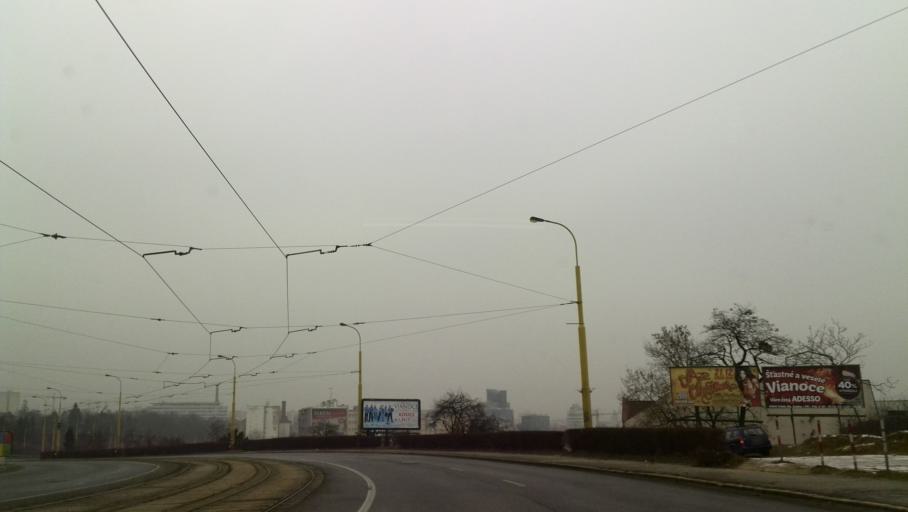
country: SK
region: Kosicky
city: Kosice
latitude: 48.7099
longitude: 21.2469
